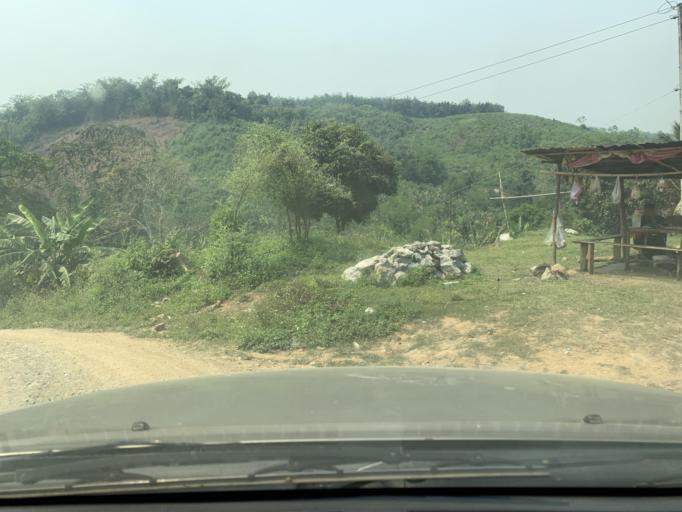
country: LA
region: Louangphabang
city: Louangphabang
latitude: 19.8819
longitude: 102.2621
